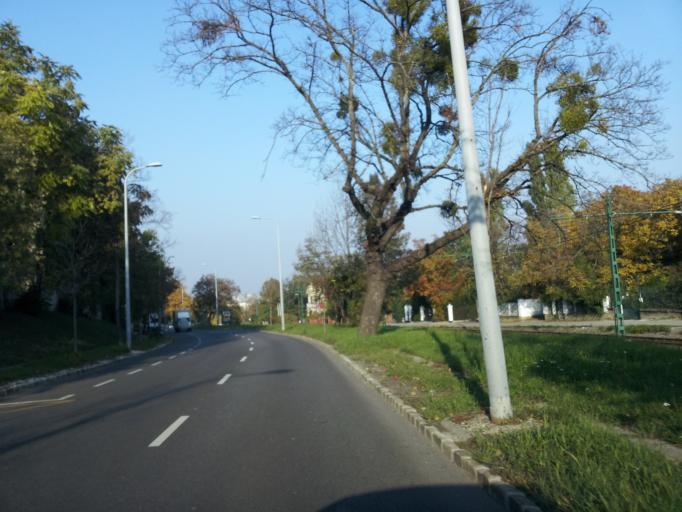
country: HU
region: Budapest
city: Budapest XII. keruelet
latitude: 47.4864
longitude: 19.0072
